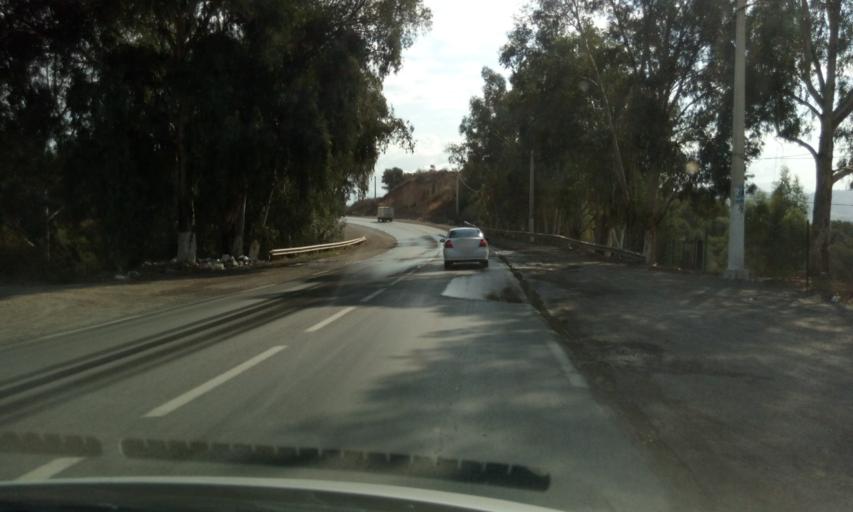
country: DZ
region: Bejaia
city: el hed
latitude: 36.6518
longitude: 4.7945
